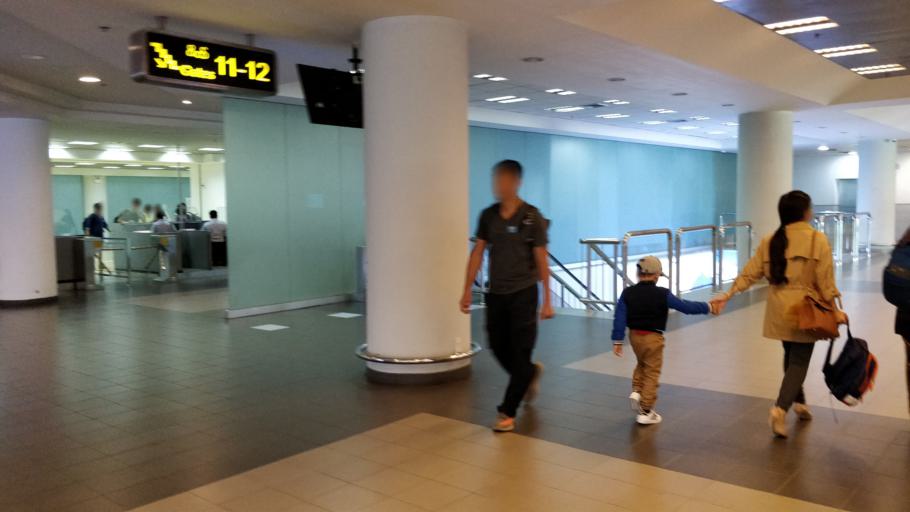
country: MM
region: Sagain
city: Sagaing
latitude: 21.7053
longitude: 95.9707
